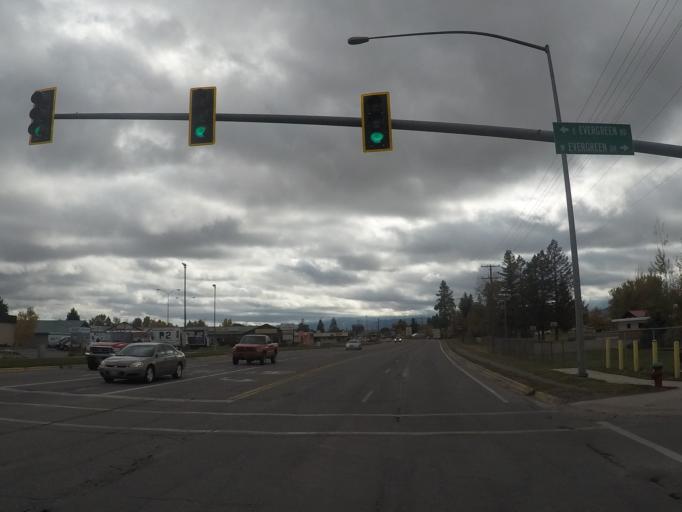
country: US
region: Montana
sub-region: Flathead County
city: Evergreen
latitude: 48.2259
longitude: -114.2764
